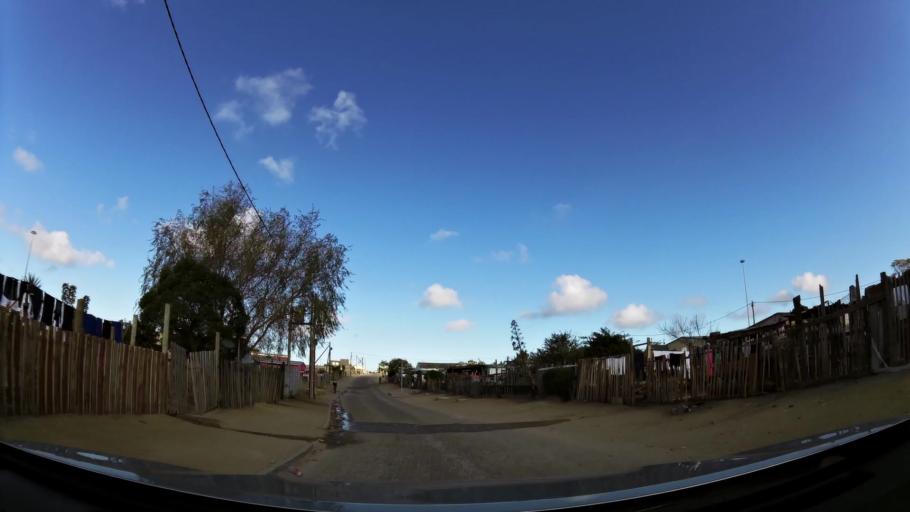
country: ZA
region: Western Cape
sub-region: Eden District Municipality
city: George
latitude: -33.9878
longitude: 22.4784
